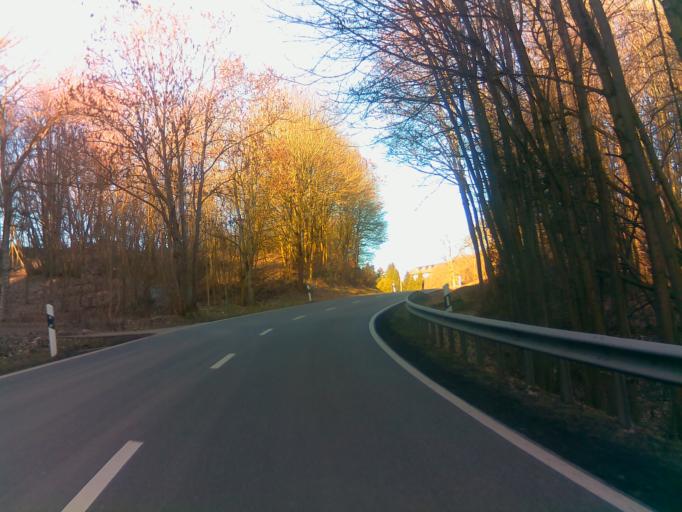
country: DE
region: Rheinland-Pfalz
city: Dannenfels
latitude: 49.6388
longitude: 7.9255
